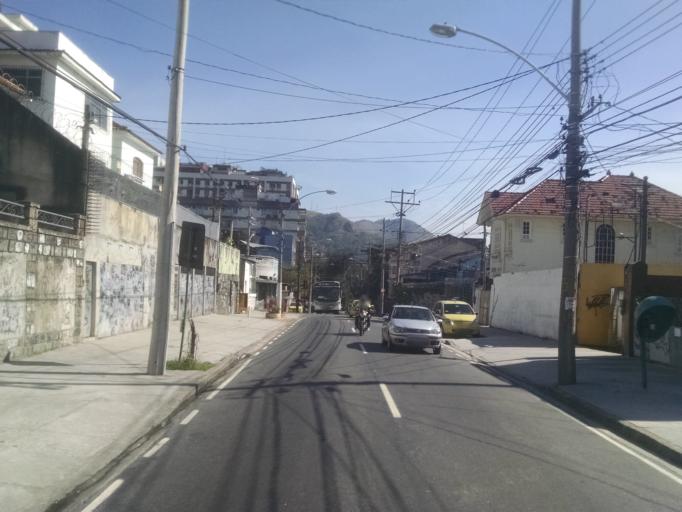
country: BR
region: Rio de Janeiro
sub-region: Rio De Janeiro
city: Rio de Janeiro
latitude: -22.9134
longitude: -43.2692
